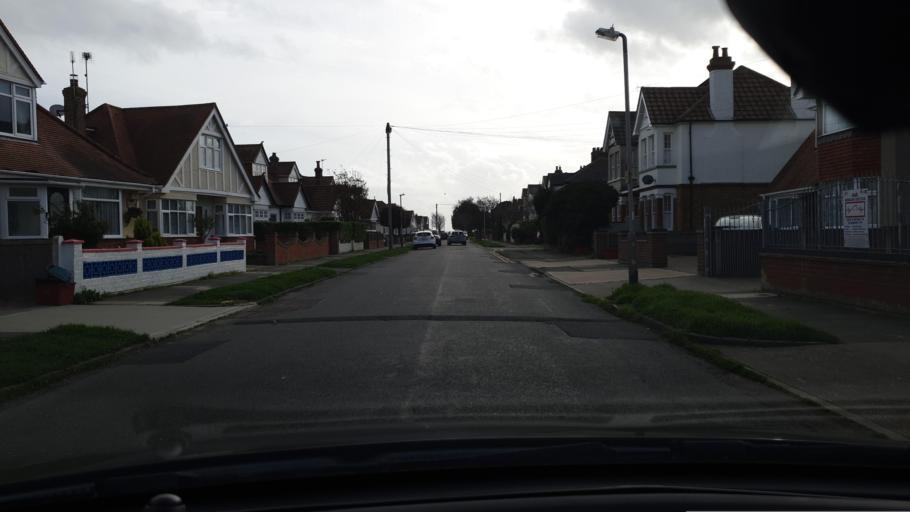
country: GB
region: England
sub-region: Essex
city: Clacton-on-Sea
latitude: 51.8033
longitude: 1.1900
